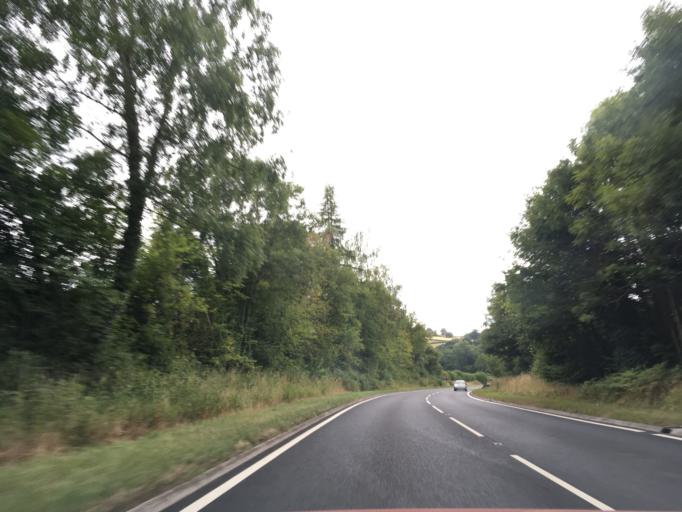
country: GB
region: Wales
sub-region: Sir Powys
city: Cray
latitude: 51.9496
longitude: -3.5195
